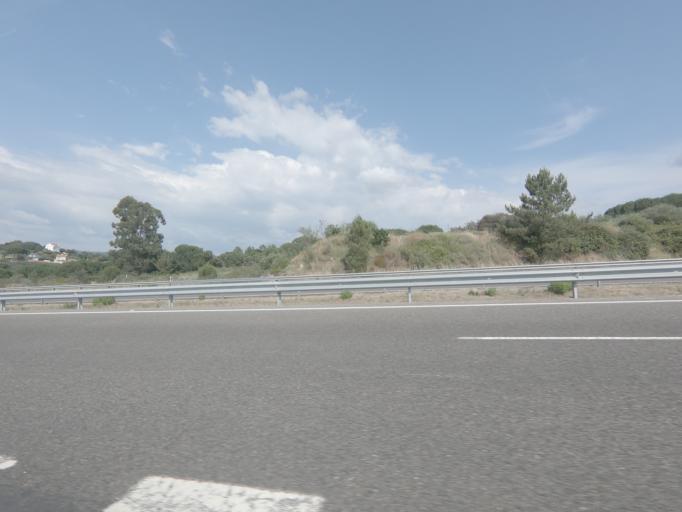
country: ES
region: Galicia
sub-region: Provincia de Ourense
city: Ourense
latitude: 42.3015
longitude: -7.8757
